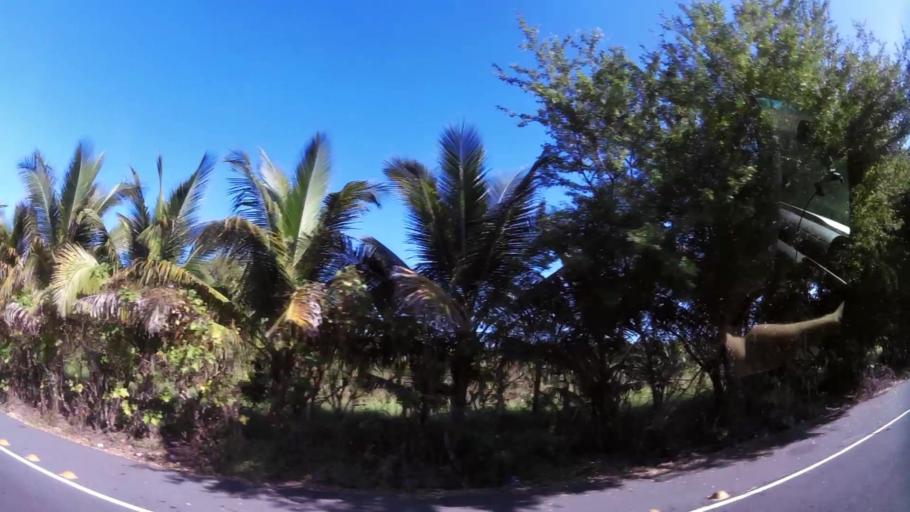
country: GT
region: Santa Rosa
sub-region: Municipio de Taxisco
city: Taxisco
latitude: 13.8837
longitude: -90.4576
